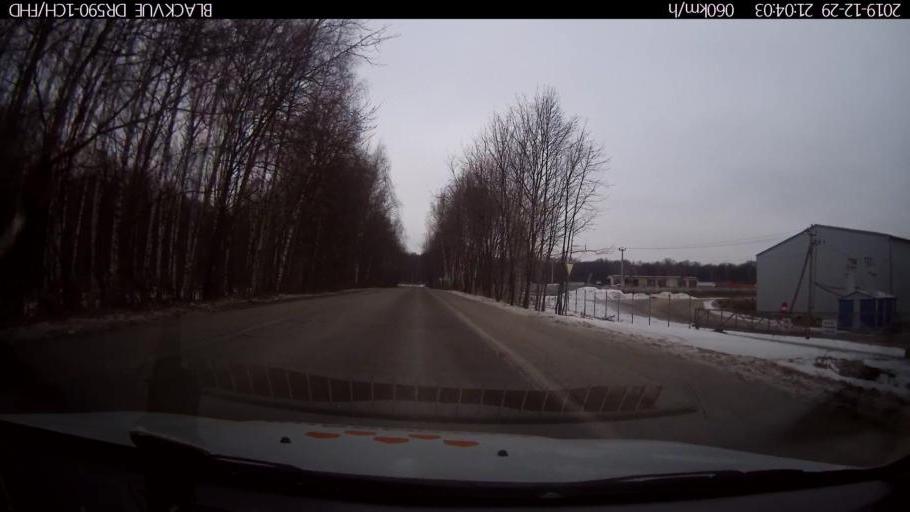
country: RU
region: Nizjnij Novgorod
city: Afonino
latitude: 56.2002
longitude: 44.0041
